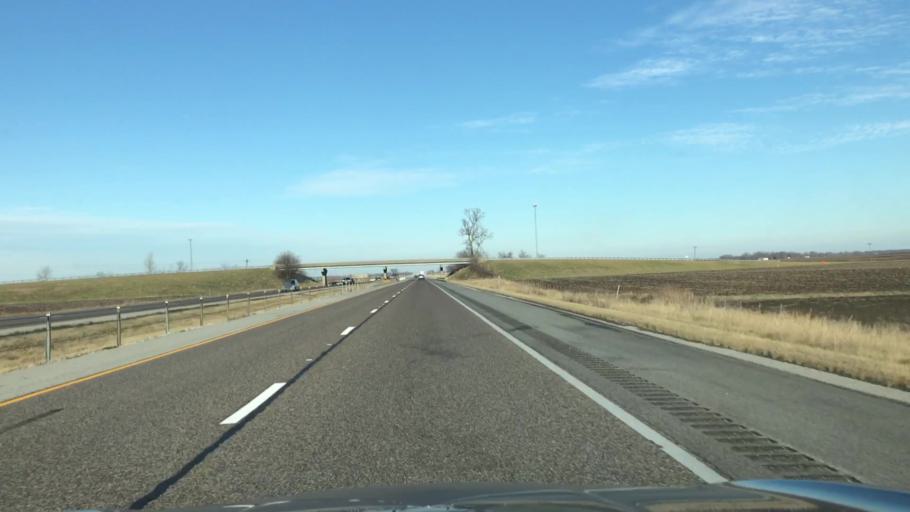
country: US
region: Illinois
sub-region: Madison County
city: Edwardsville
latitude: 38.8293
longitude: -89.8800
